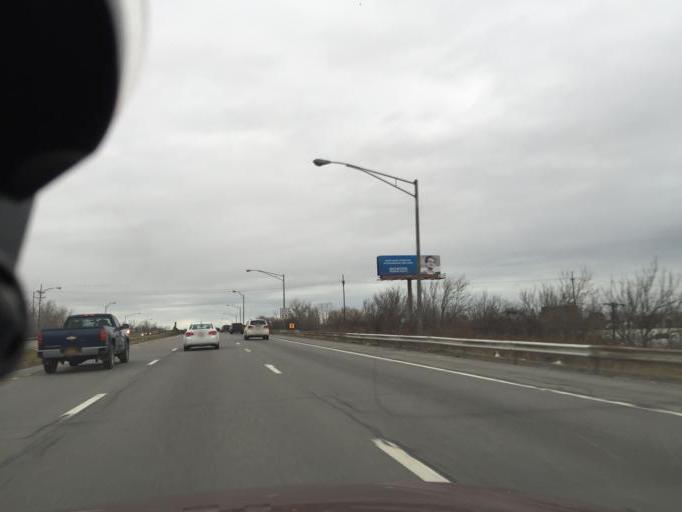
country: US
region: New York
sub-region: Monroe County
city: North Gates
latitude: 43.1701
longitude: -77.6830
